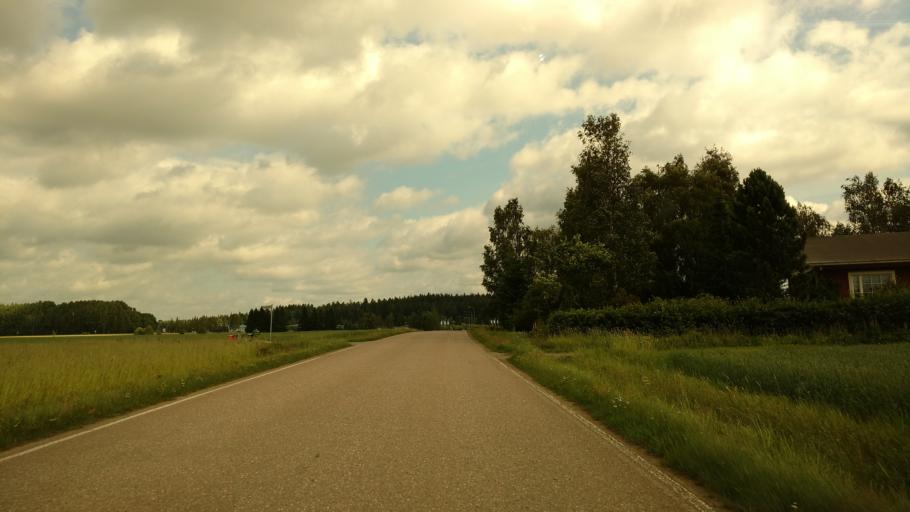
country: FI
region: Haeme
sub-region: Forssa
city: Ypaejae
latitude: 60.7913
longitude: 23.2740
